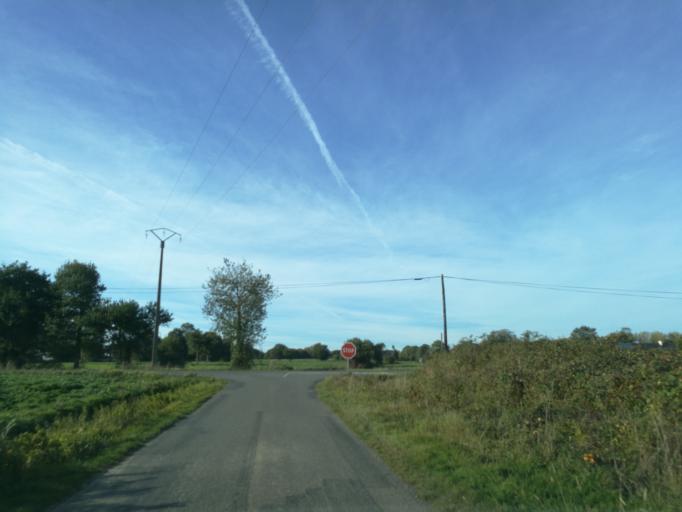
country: FR
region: Brittany
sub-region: Departement d'Ille-et-Vilaine
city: Bedee
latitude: 48.2051
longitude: -1.9560
